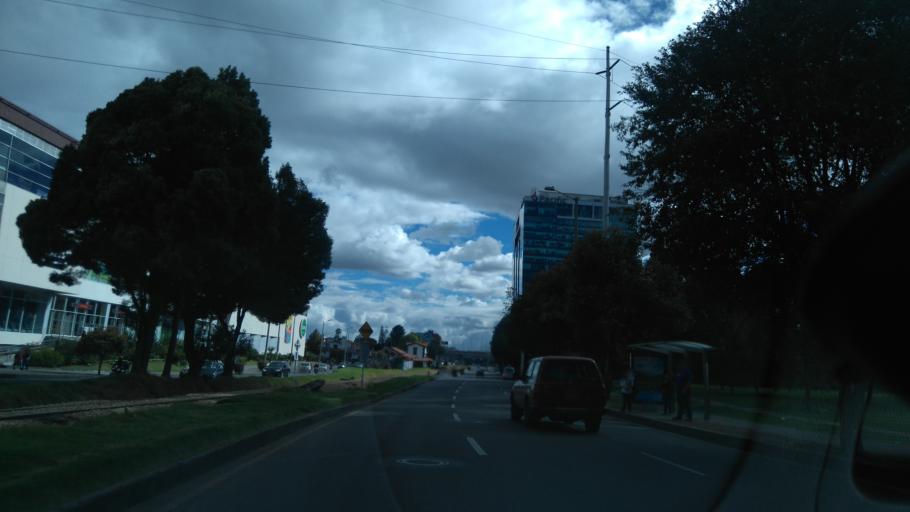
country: CO
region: Bogota D.C.
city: Barrio San Luis
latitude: 4.6921
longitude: -74.0359
